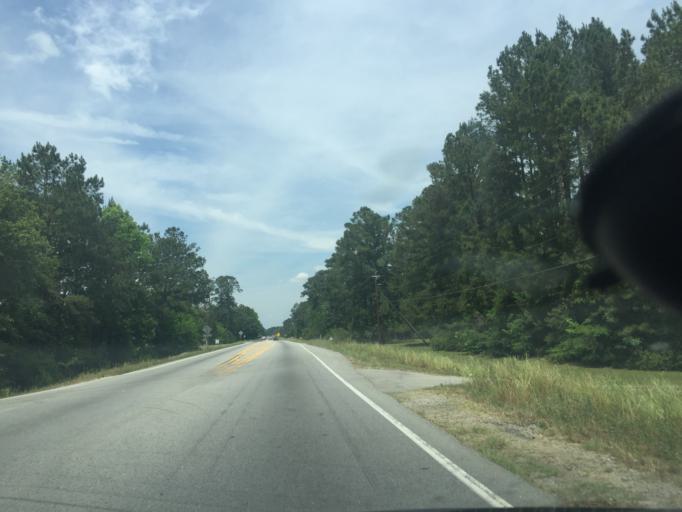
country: US
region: Georgia
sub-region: Chatham County
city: Bloomingdale
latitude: 32.1799
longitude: -81.3961
